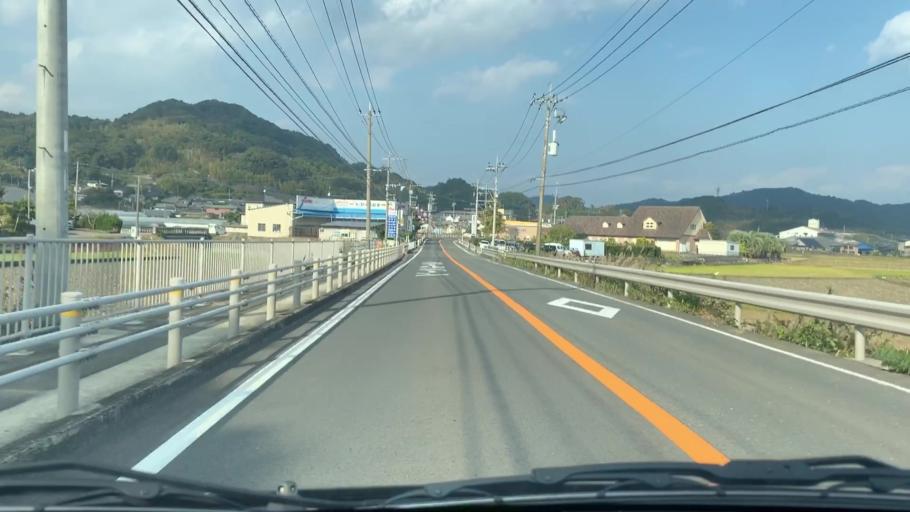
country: JP
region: Nagasaki
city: Togitsu
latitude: 32.9432
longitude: 129.7821
